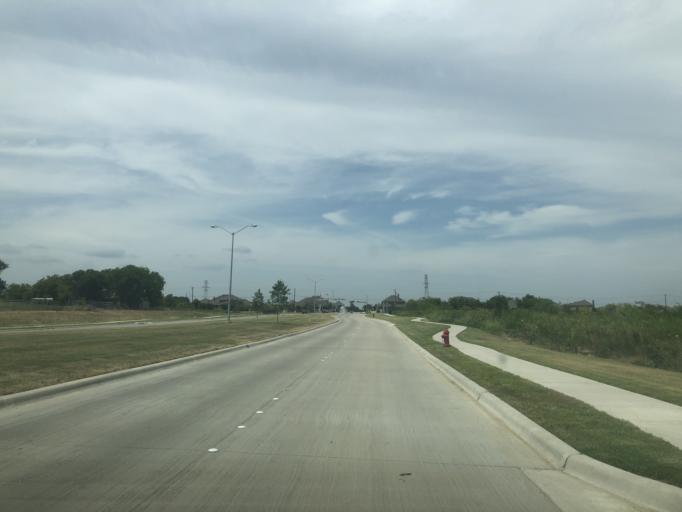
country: US
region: Texas
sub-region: Tarrant County
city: Saginaw
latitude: 32.8812
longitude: -97.3550
